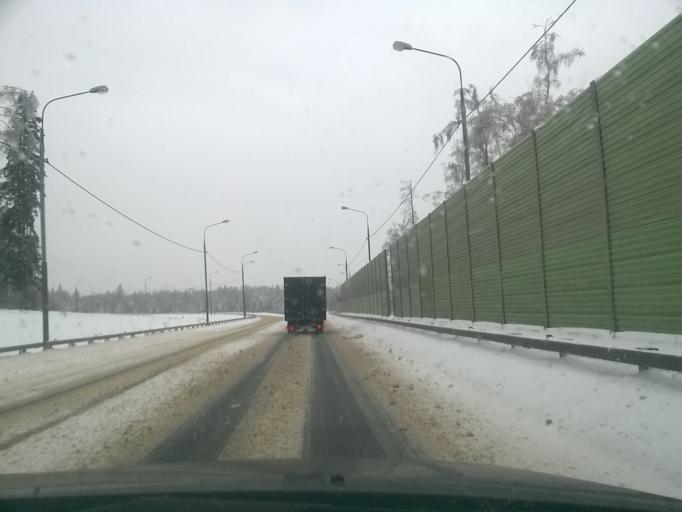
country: RU
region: Moskovskaya
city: Selyatino
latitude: 55.5192
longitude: 36.9948
